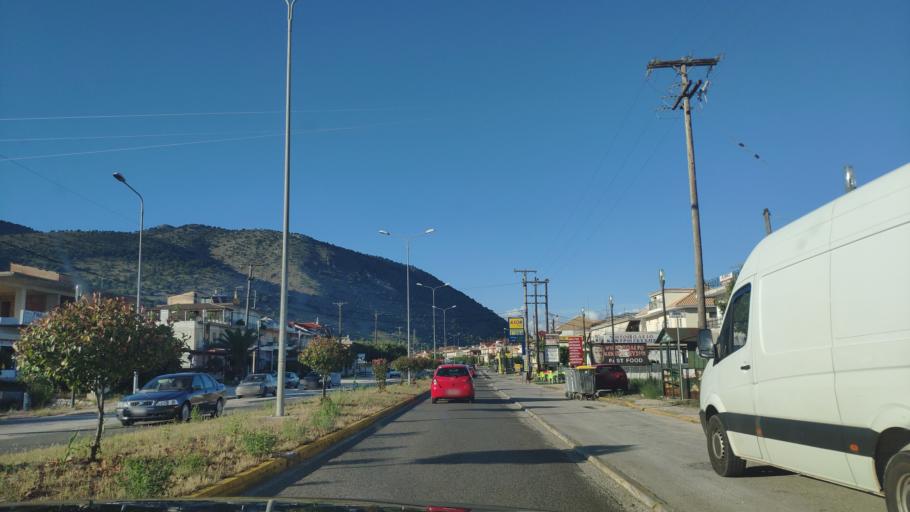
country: GR
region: Epirus
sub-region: Nomos Prevezis
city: Louros
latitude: 39.1659
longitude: 20.7564
